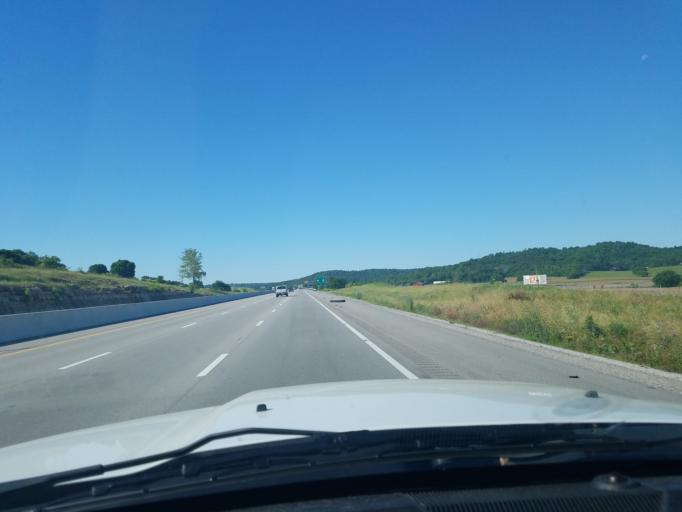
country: US
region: Kentucky
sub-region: Hart County
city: Horse Cave
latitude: 37.2193
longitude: -85.9344
